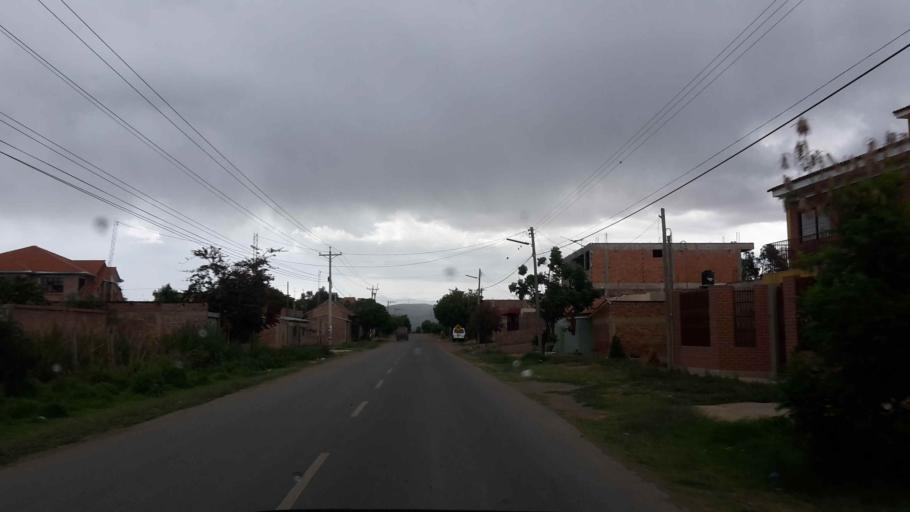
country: BO
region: Cochabamba
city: Tarata
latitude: -17.5852
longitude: -66.0515
